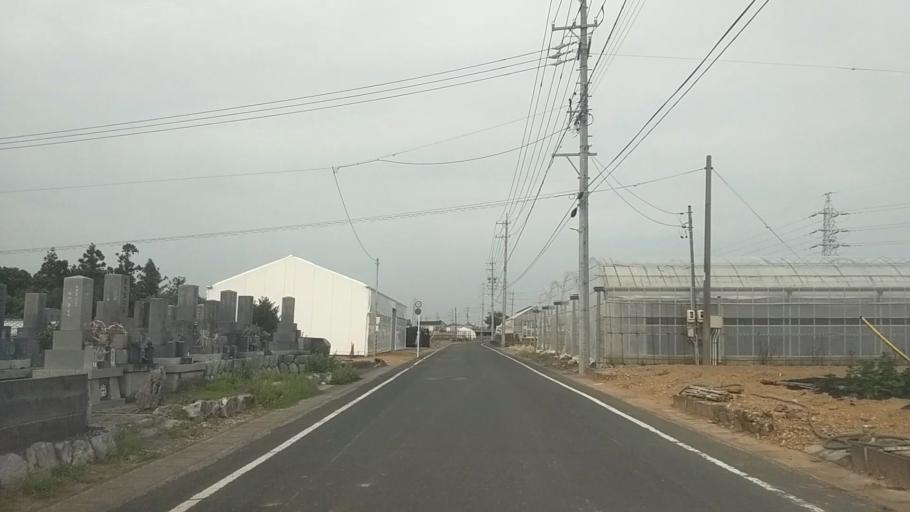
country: JP
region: Shizuoka
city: Kosai-shi
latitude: 34.7567
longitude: 137.6171
